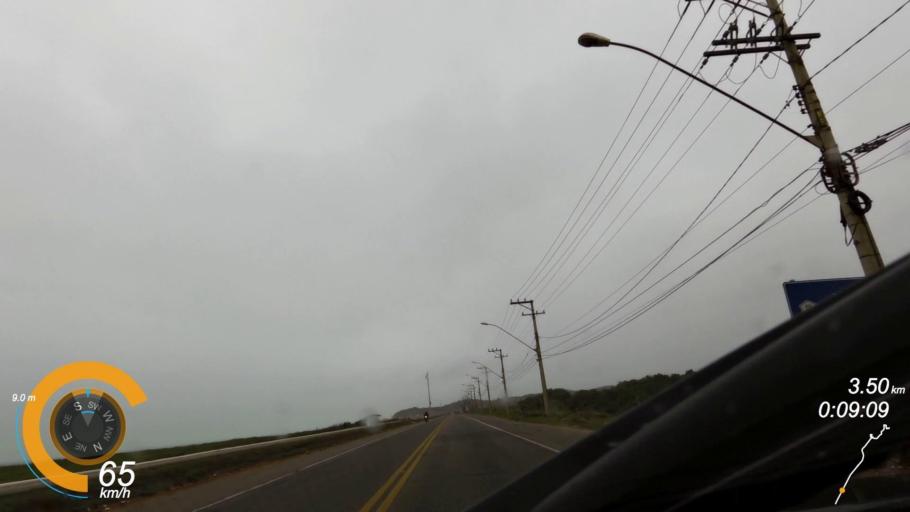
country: BR
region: Espirito Santo
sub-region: Guarapari
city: Guarapari
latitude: -20.6907
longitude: -40.5110
